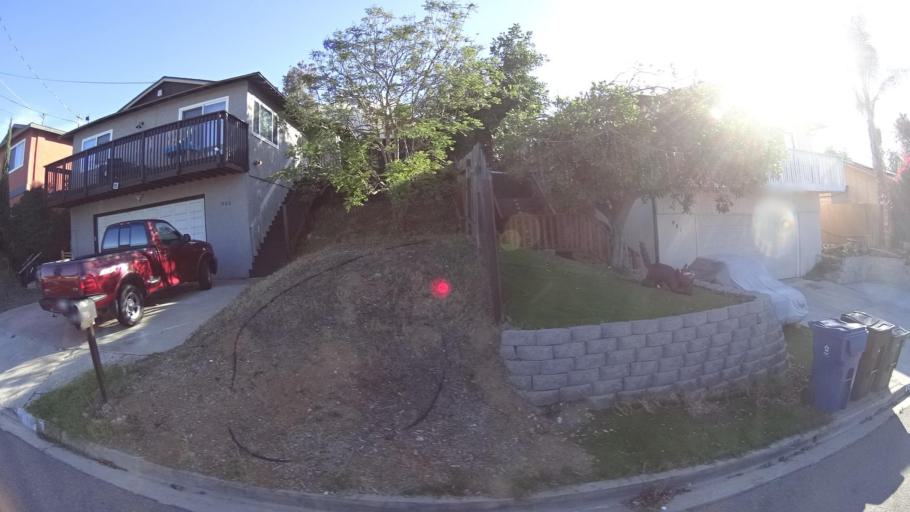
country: US
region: California
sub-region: San Diego County
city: La Presa
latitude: 32.7132
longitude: -116.9896
